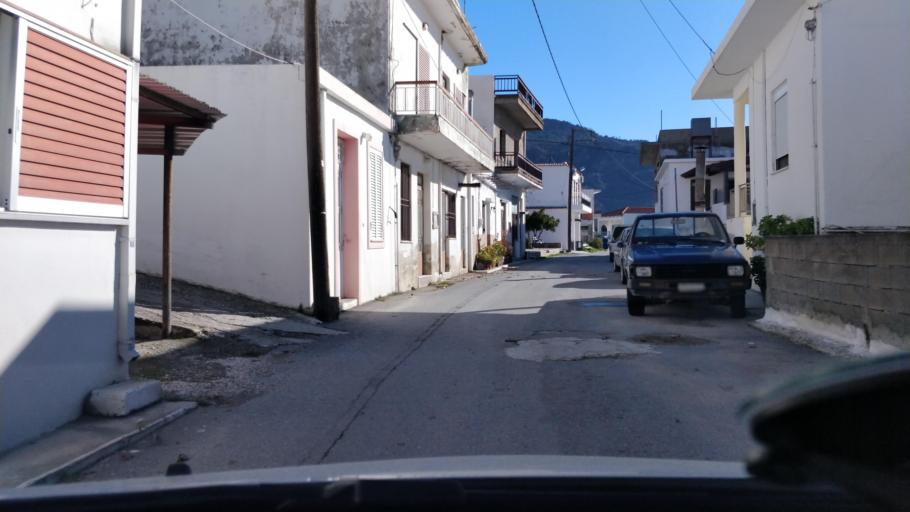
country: GR
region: Crete
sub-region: Nomos Lasithiou
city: Kritsa
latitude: 35.0800
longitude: 25.5870
